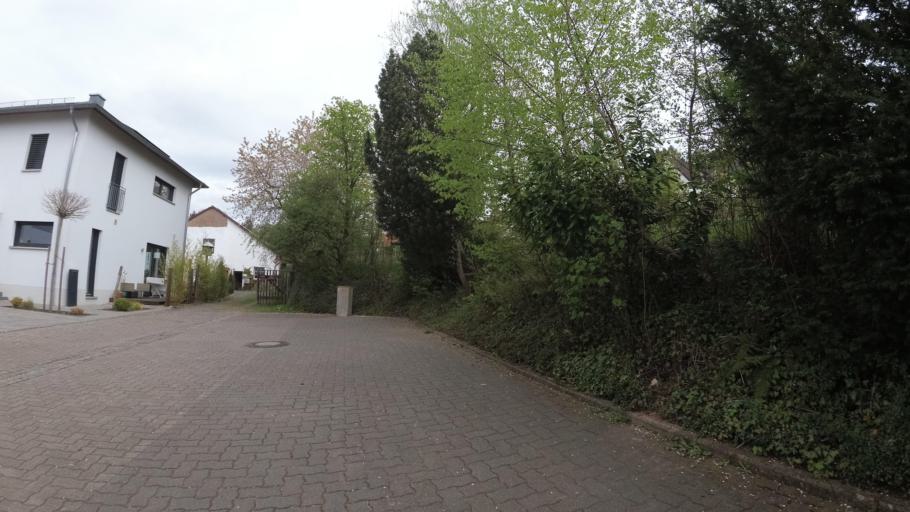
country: DE
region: Rheinland-Pfalz
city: Zweibrucken
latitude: 49.2472
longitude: 7.3777
